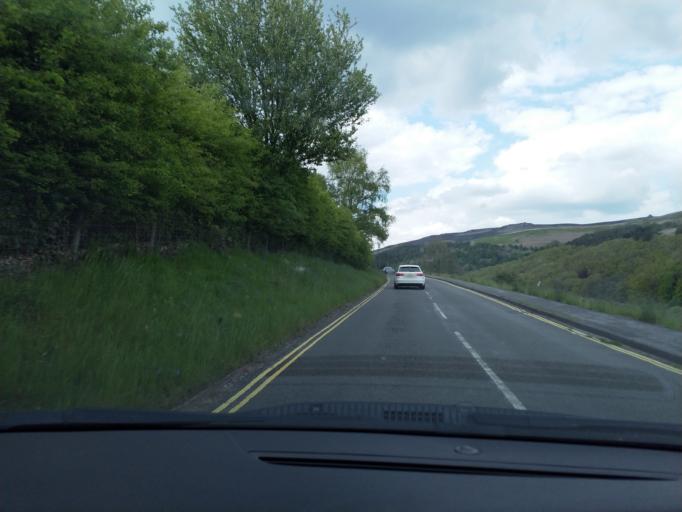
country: GB
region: England
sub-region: Derbyshire
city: Hope Valley
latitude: 53.3768
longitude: -1.7145
